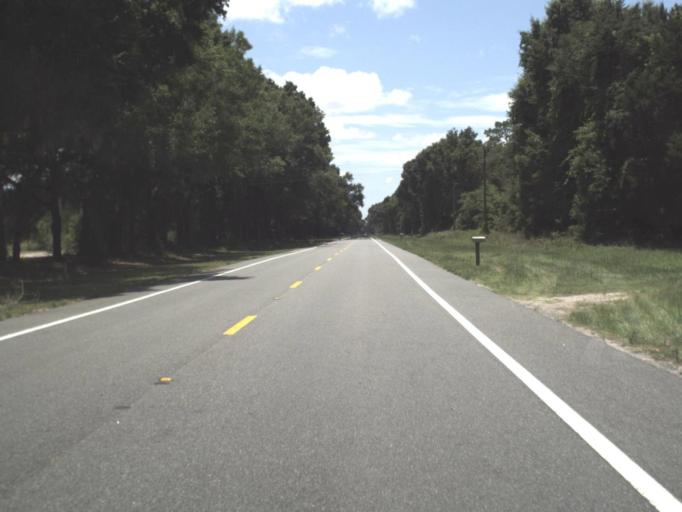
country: US
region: Florida
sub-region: Dixie County
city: Cross City
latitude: 29.8586
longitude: -82.9616
